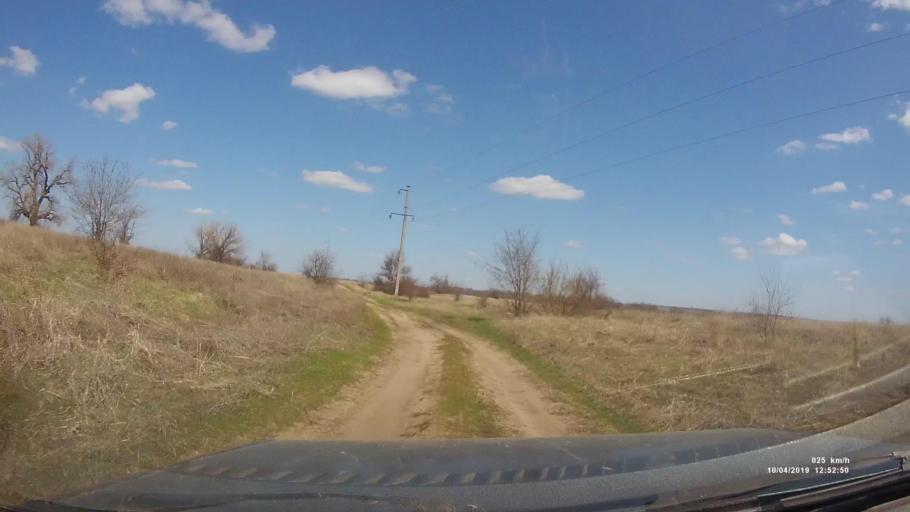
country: RU
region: Rostov
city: Masalovka
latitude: 48.3623
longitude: 40.2188
